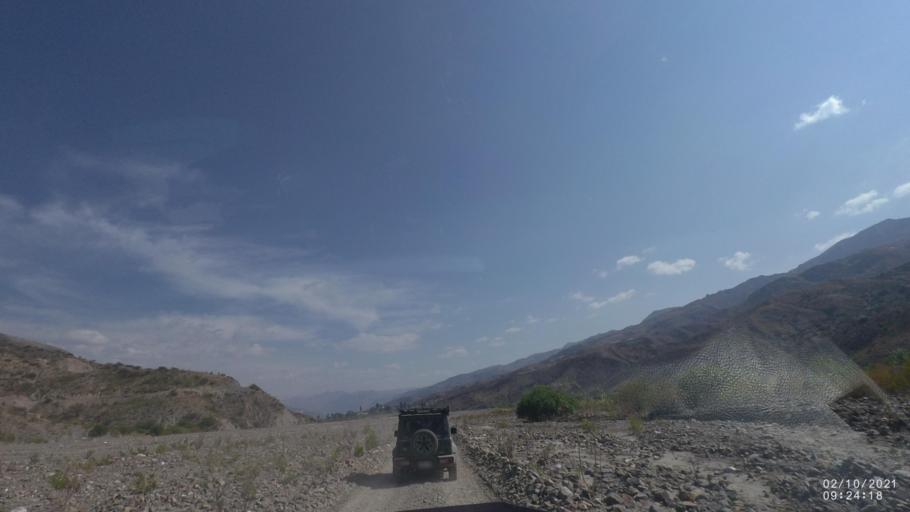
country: BO
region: Cochabamba
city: Irpa Irpa
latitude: -17.8644
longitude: -66.3125
